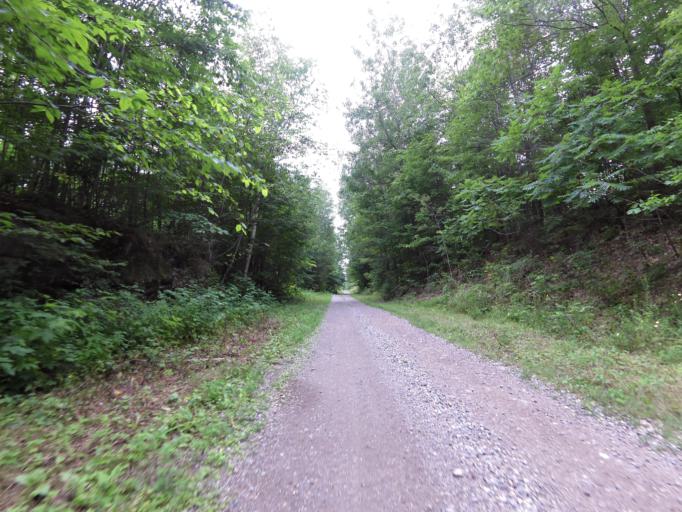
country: CA
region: Ontario
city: Perth
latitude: 44.8120
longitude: -76.6080
